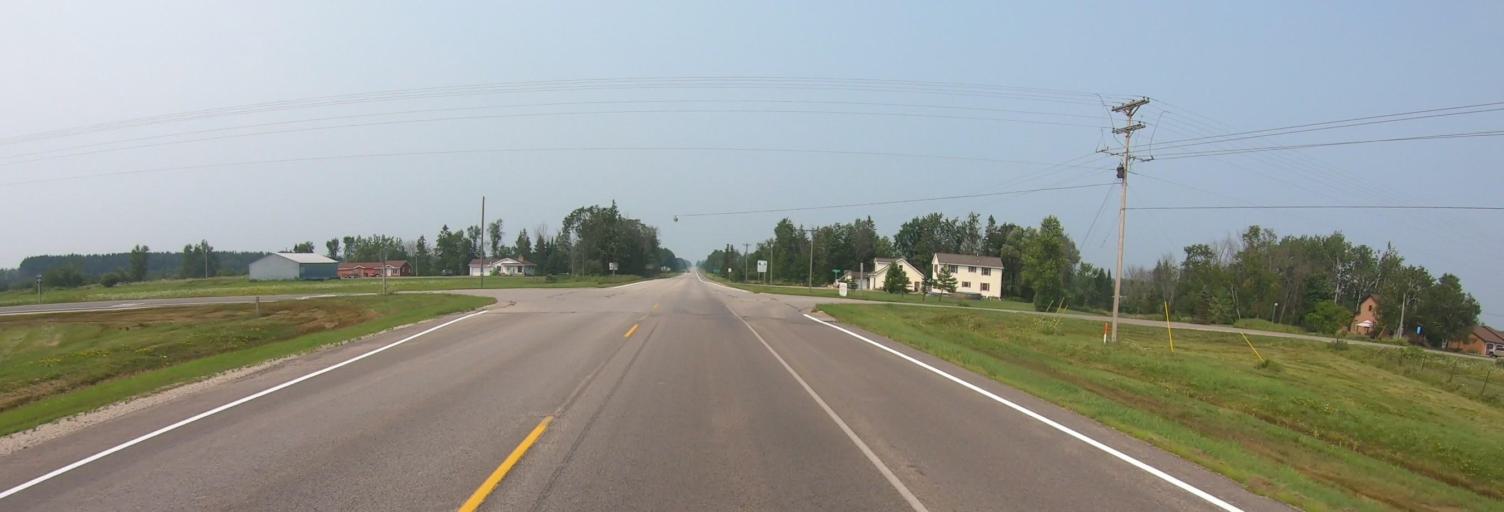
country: US
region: Michigan
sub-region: Chippewa County
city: Sault Ste. Marie
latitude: 46.1866
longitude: -84.3635
